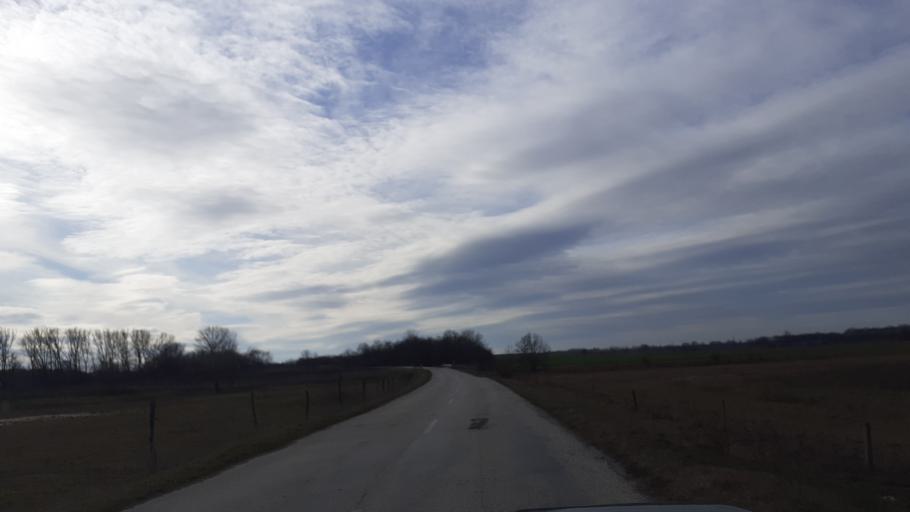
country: HU
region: Fejer
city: Kaloz
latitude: 46.9093
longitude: 18.5309
